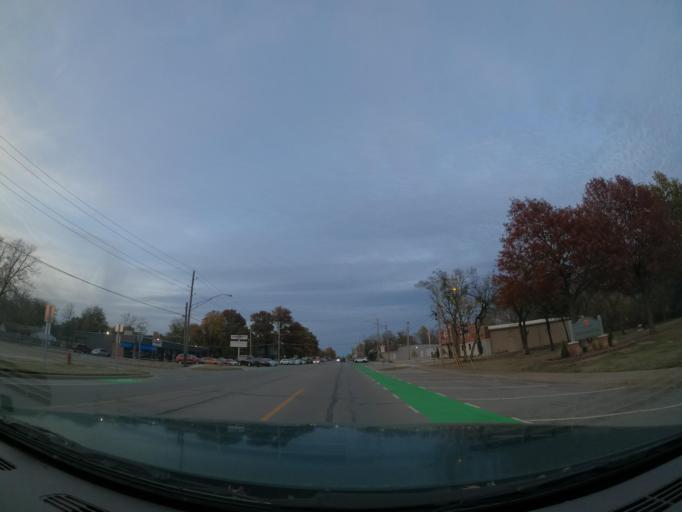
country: US
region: Oklahoma
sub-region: Tulsa County
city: Broken Arrow
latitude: 36.0421
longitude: -95.7908
